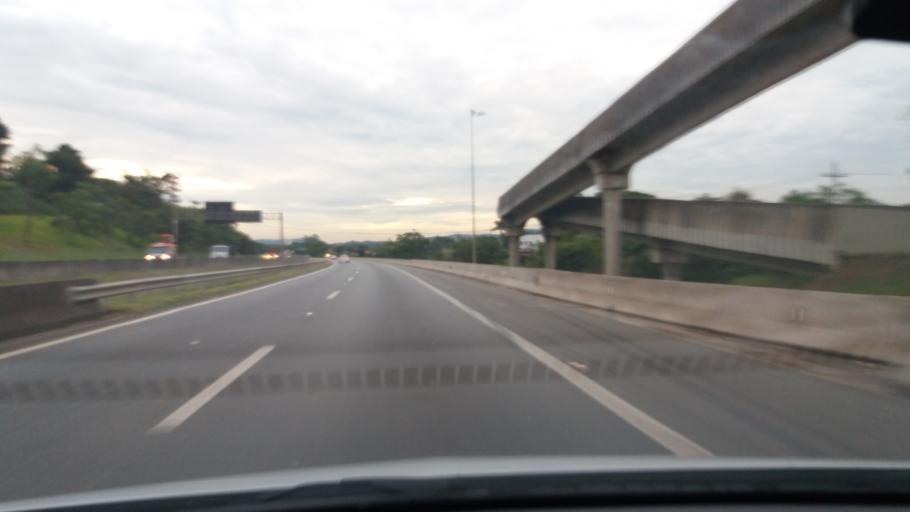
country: BR
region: Sao Paulo
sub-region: Atibaia
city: Atibaia
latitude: -23.1074
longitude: -46.5064
